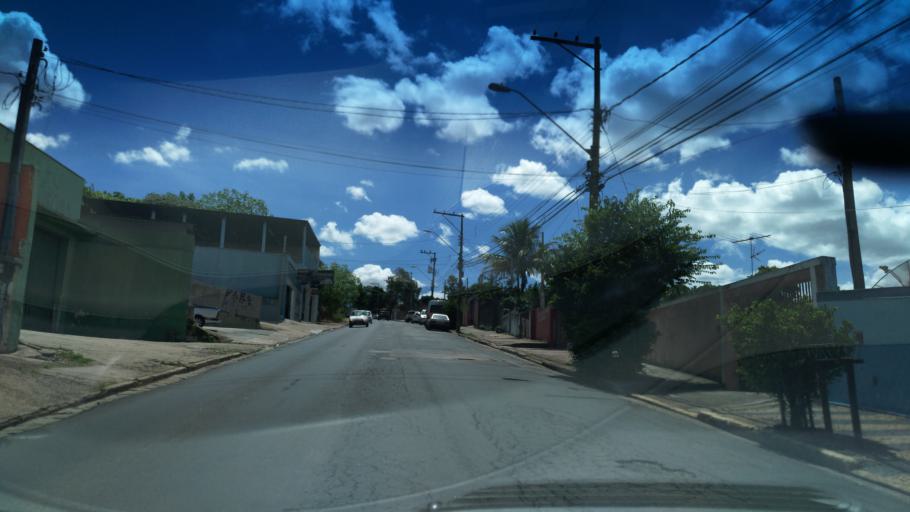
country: BR
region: Sao Paulo
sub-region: Valinhos
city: Valinhos
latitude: -22.9608
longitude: -47.0046
